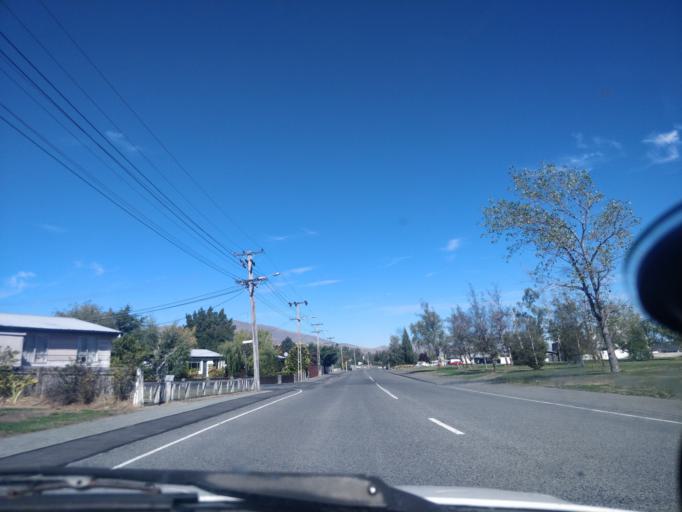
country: NZ
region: Canterbury
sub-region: Timaru District
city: Pleasant Point
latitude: -44.2545
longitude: 170.1015
